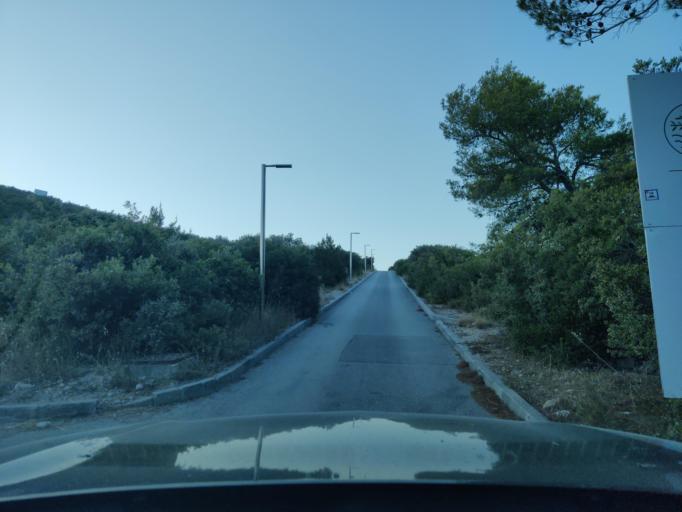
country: HR
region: Sibensko-Kniniska
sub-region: Grad Sibenik
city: Tisno
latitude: 43.8097
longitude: 15.6282
